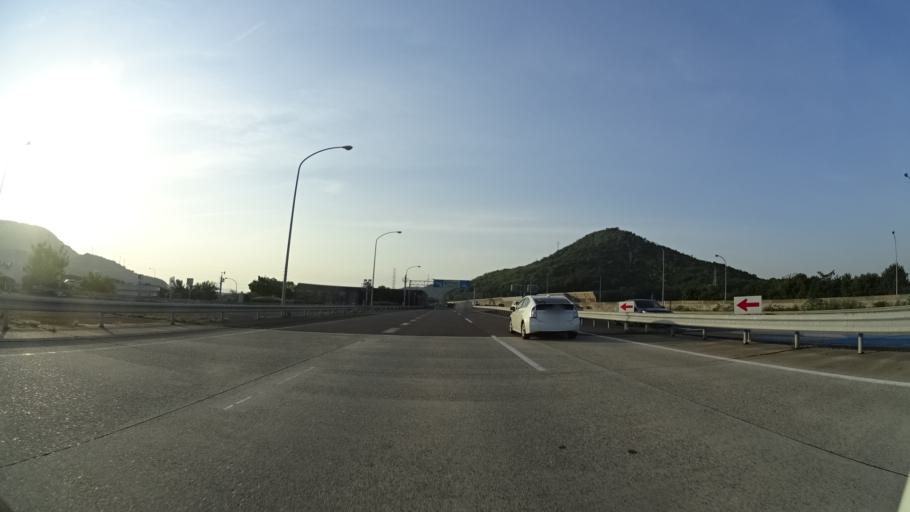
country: JP
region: Kagawa
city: Sakaidecho
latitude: 34.2977
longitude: 133.8439
